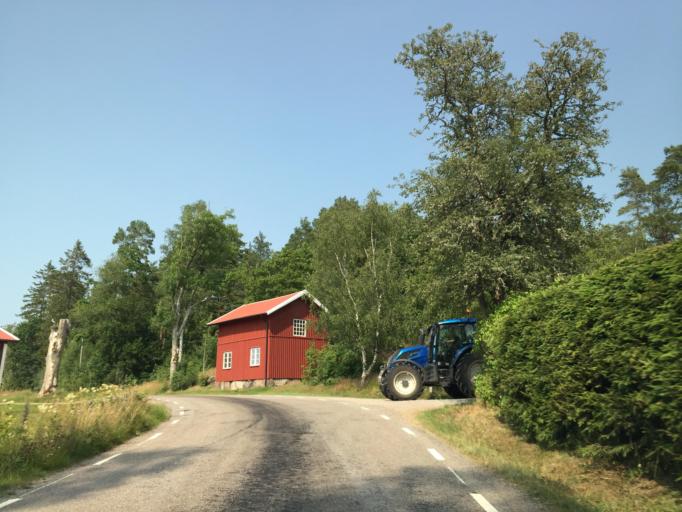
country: SE
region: Vaestra Goetaland
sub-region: Trollhattan
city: Sjuntorp
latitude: 58.3255
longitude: 12.1239
